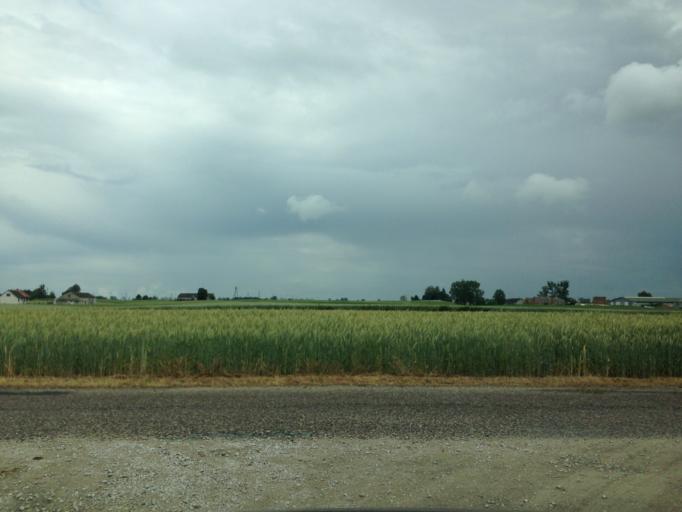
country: PL
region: Kujawsko-Pomorskie
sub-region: Powiat brodnicki
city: Gorzno
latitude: 53.1975
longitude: 19.5999
